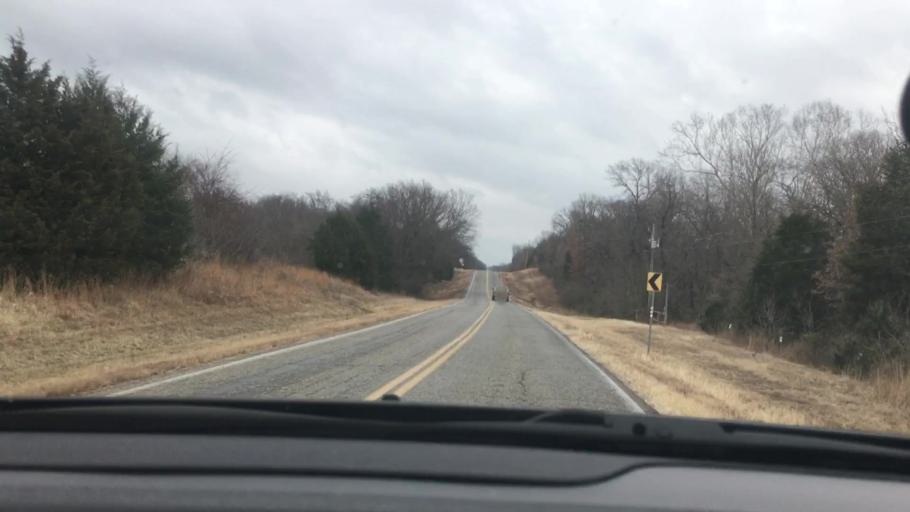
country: US
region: Oklahoma
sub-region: Johnston County
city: Tishomingo
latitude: 34.2088
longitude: -96.6351
